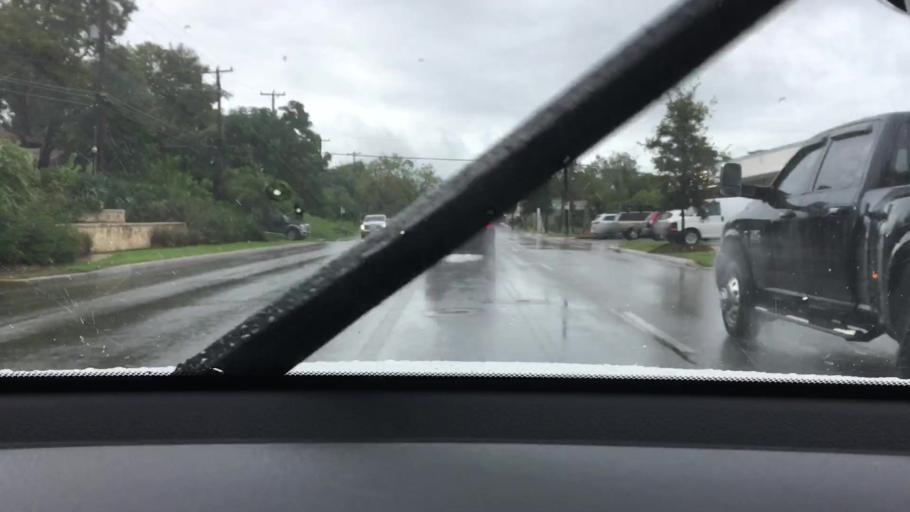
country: US
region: Texas
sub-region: Bexar County
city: Alamo Heights
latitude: 29.4870
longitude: -98.4665
